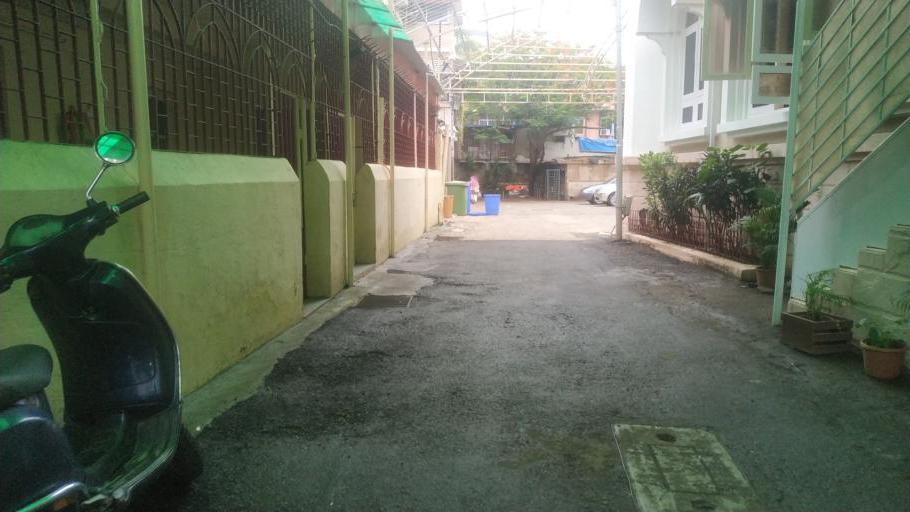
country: IN
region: Maharashtra
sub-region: Mumbai Suburban
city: Mumbai
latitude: 19.0549
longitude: 72.8338
